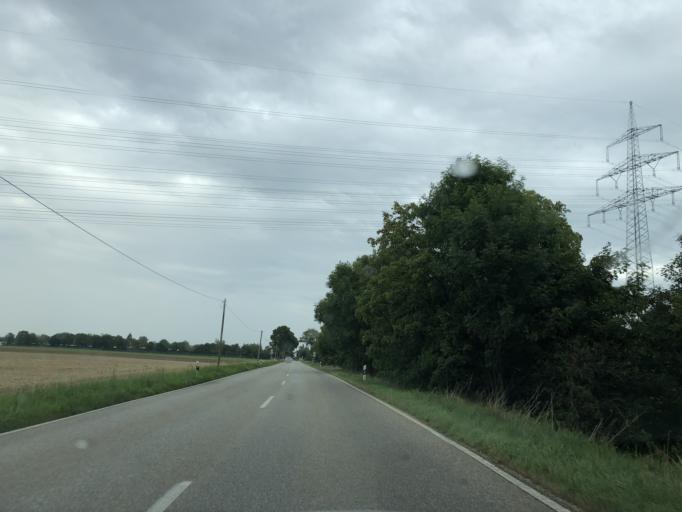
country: DE
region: Bavaria
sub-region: Upper Bavaria
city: Eching
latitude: 48.2868
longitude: 11.6134
